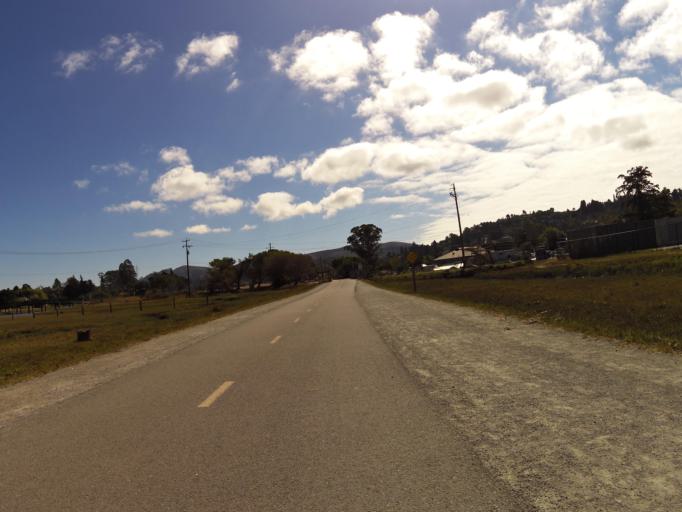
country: US
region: California
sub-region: Marin County
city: Strawberry
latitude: 37.8981
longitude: -122.5264
